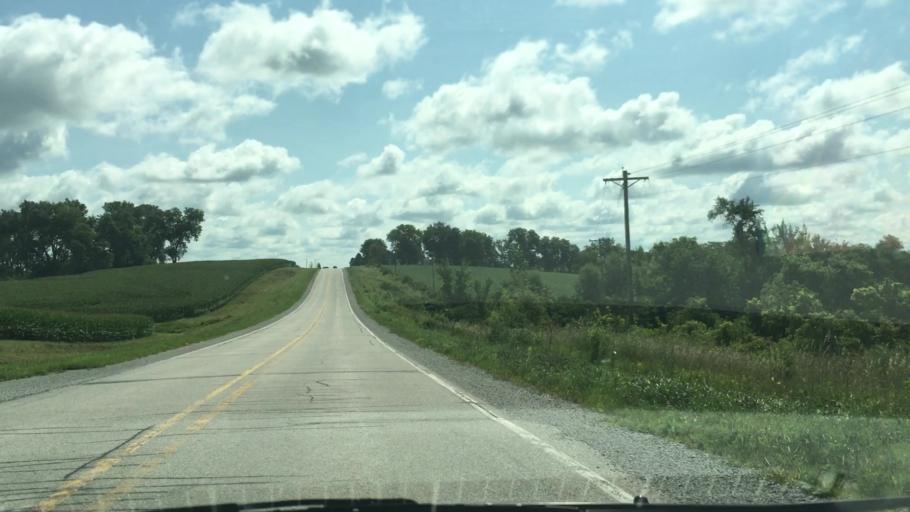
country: US
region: Iowa
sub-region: Johnson County
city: Solon
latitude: 41.8310
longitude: -91.4639
